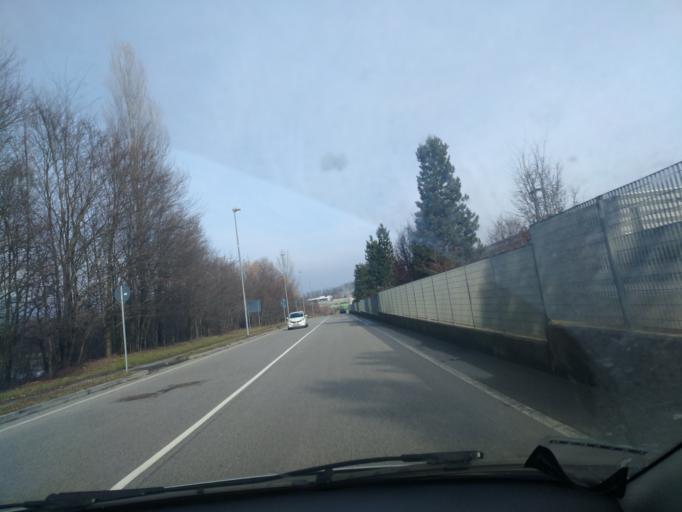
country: IT
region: Lombardy
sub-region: Provincia di Como
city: Lurago d'Erba
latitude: 45.7625
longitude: 9.2180
